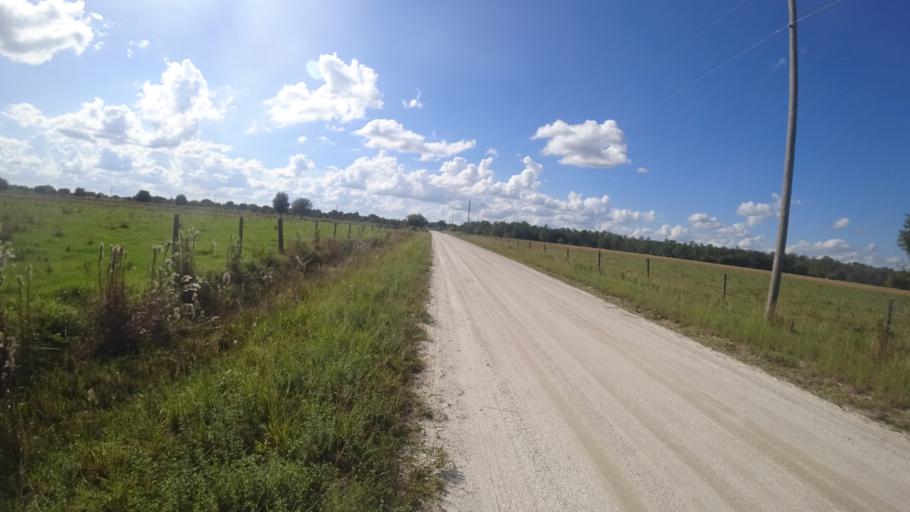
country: US
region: Florida
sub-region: Hardee County
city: Wauchula
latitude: 27.4623
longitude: -82.0532
